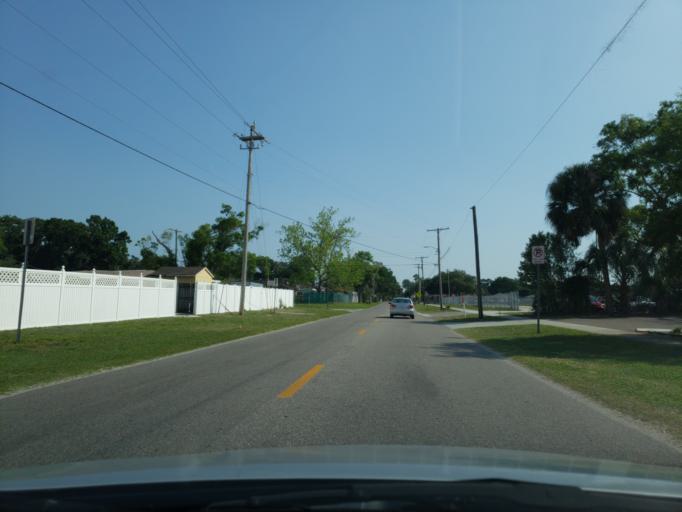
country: US
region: Florida
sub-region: Hillsborough County
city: Egypt Lake-Leto
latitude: 27.9762
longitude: -82.4931
